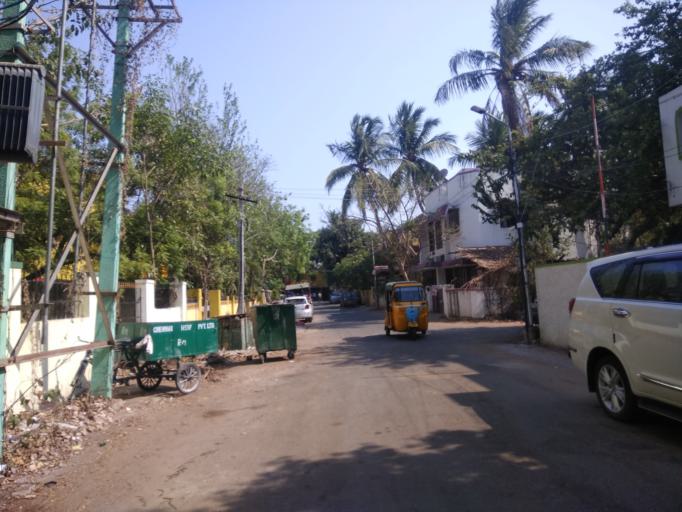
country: IN
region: Tamil Nadu
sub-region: Kancheepuram
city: Perungudi
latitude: 12.9866
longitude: 80.2298
